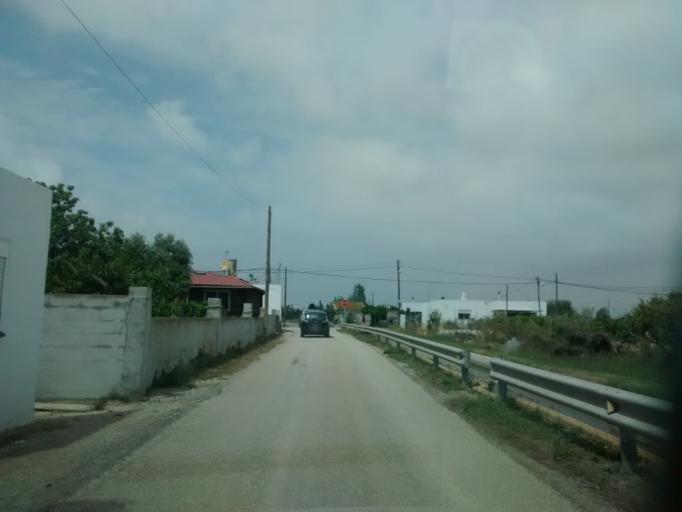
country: ES
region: Catalonia
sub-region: Provincia de Tarragona
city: Deltebre
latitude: 40.6719
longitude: 0.7511
